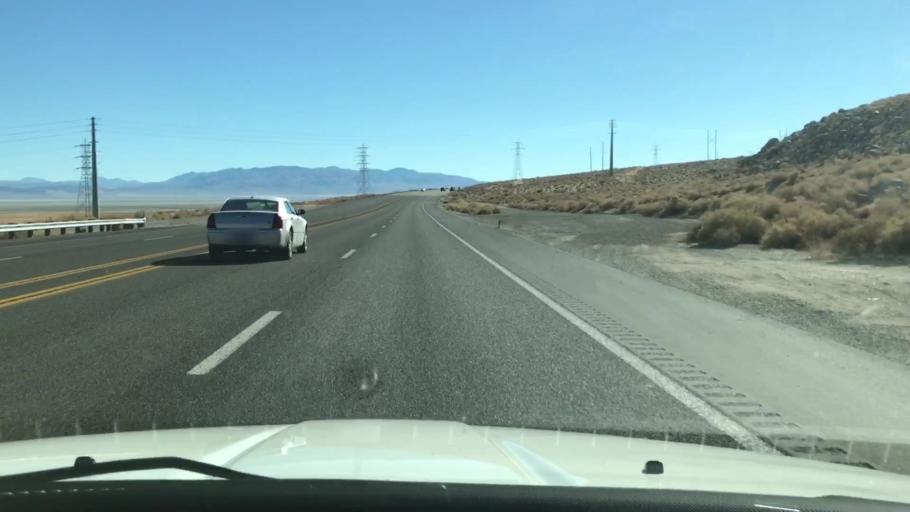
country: US
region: California
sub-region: Inyo County
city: Lone Pine
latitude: 36.5130
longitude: -118.0353
